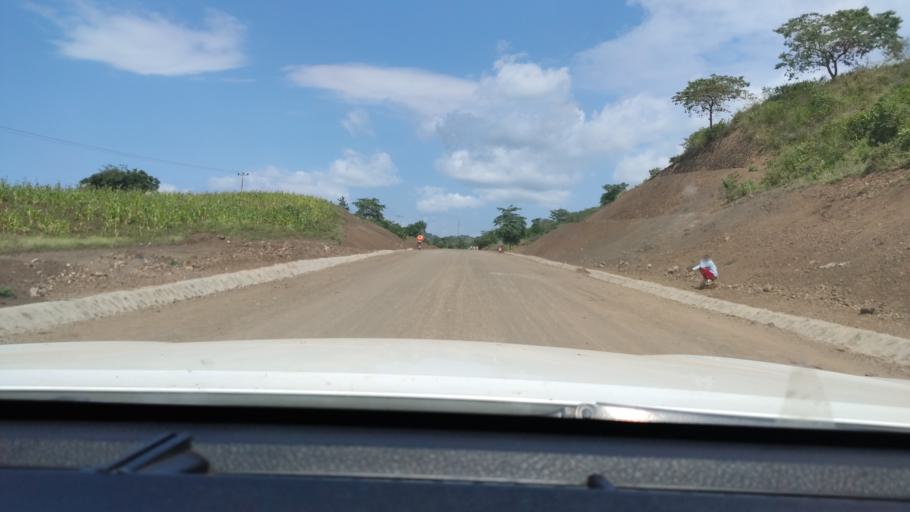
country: ET
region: Southern Nations, Nationalities, and People's Region
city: Felege Neway
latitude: 6.3916
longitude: 37.0689
